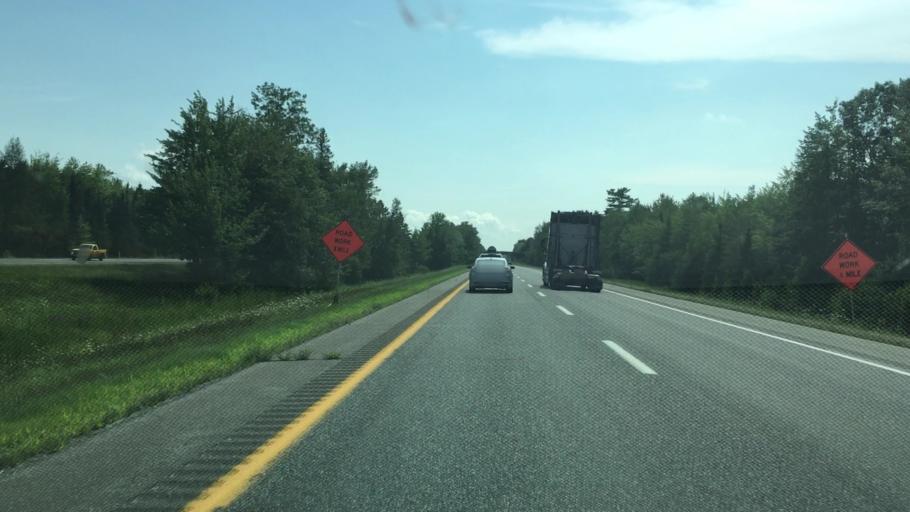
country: US
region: Maine
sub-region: Penobscot County
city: Veazie
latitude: 44.8504
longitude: -68.7273
